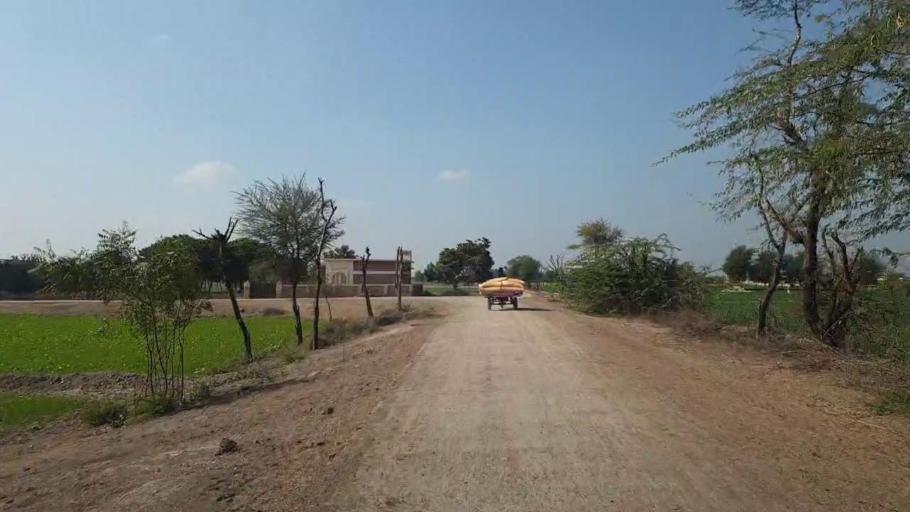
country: PK
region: Sindh
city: Shahdadpur
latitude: 26.0412
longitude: 68.5835
